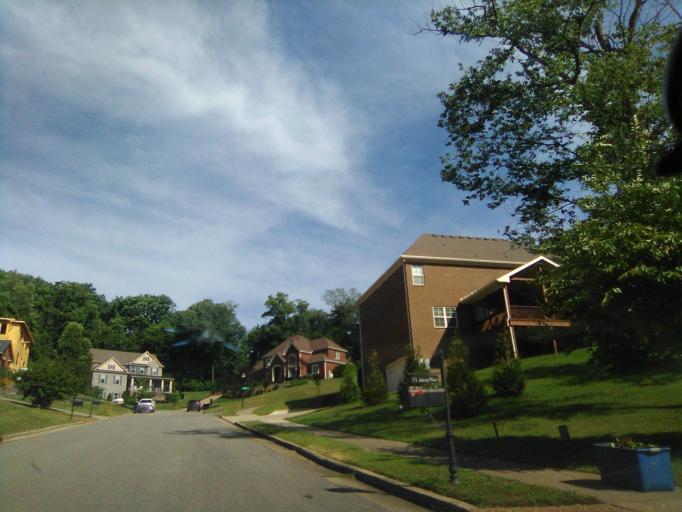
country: US
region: Tennessee
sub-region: Davidson County
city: Belle Meade
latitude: 36.1133
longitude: -86.9127
